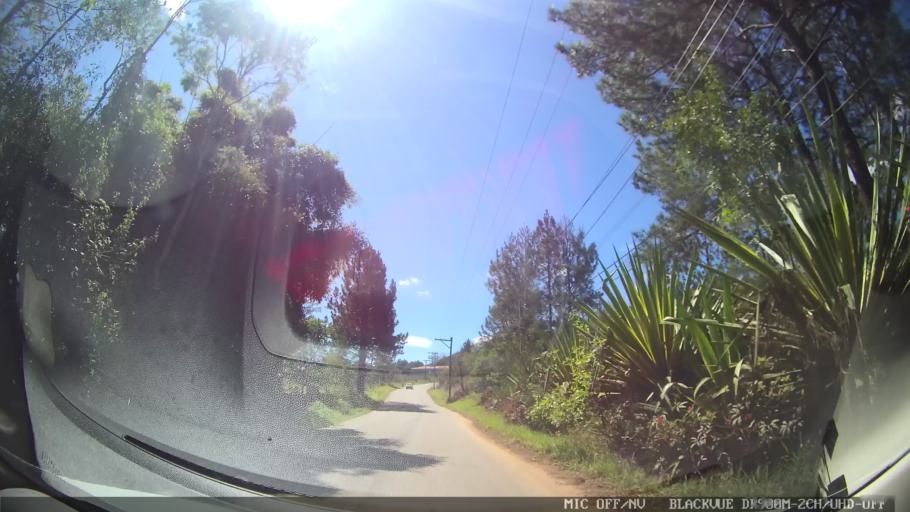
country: BR
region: Sao Paulo
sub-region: Jarinu
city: Jarinu
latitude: -23.1591
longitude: -46.7279
